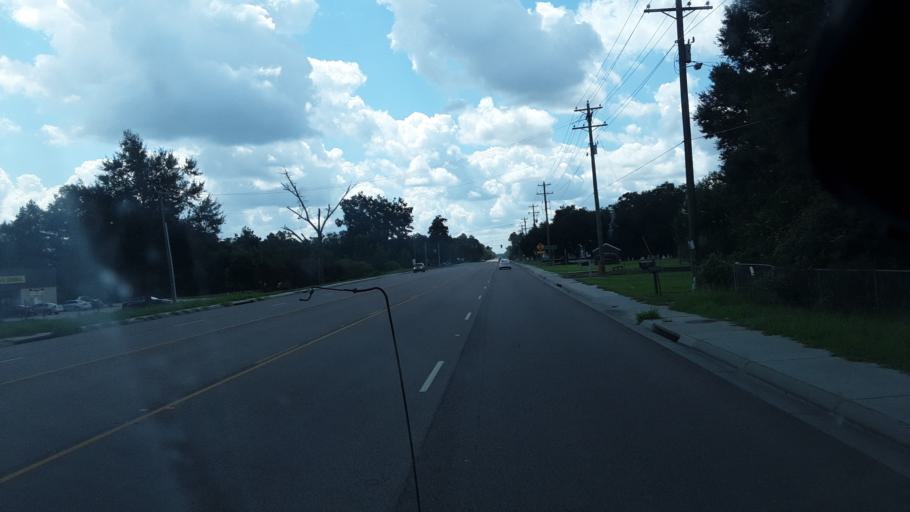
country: US
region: South Carolina
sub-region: Berkeley County
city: Moncks Corner
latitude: 33.1551
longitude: -80.0592
